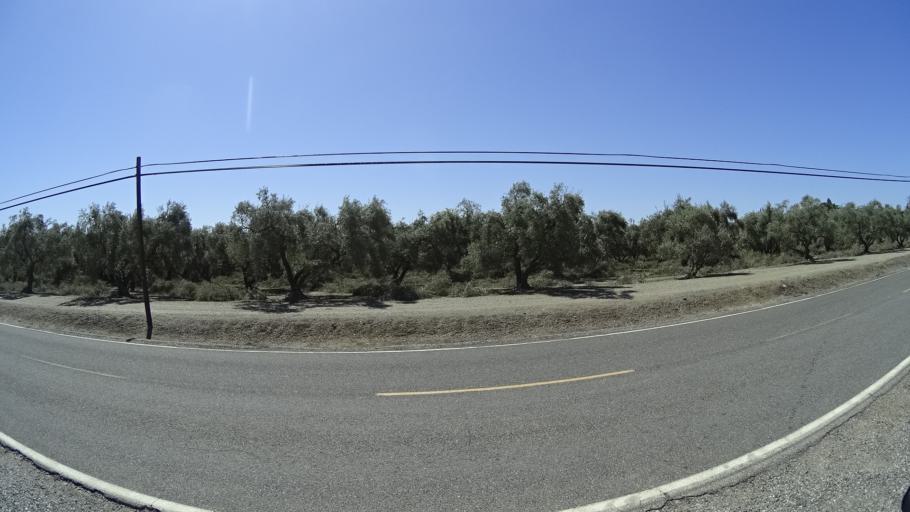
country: US
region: California
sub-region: Glenn County
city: Orland
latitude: 39.7107
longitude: -122.1315
